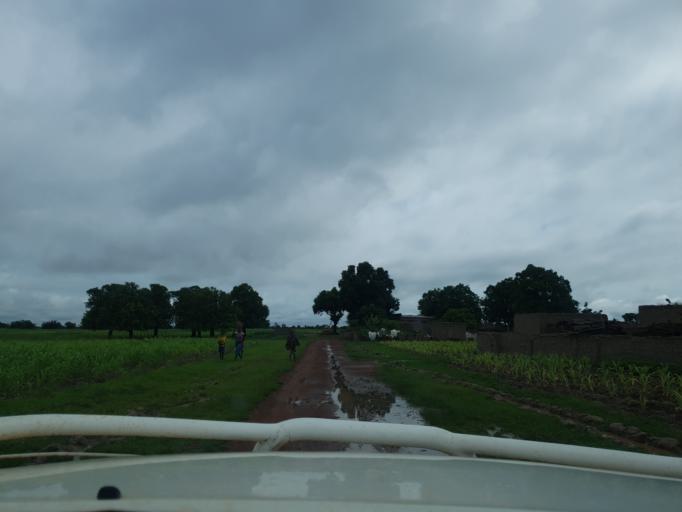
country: ML
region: Segou
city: Bla
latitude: 12.7998
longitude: -5.6056
